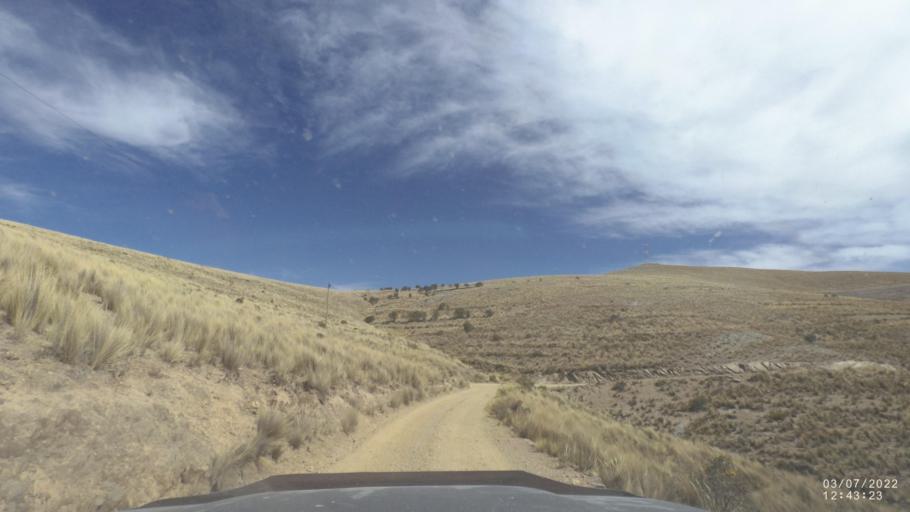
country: BO
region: Cochabamba
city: Irpa Irpa
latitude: -17.7827
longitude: -66.6295
